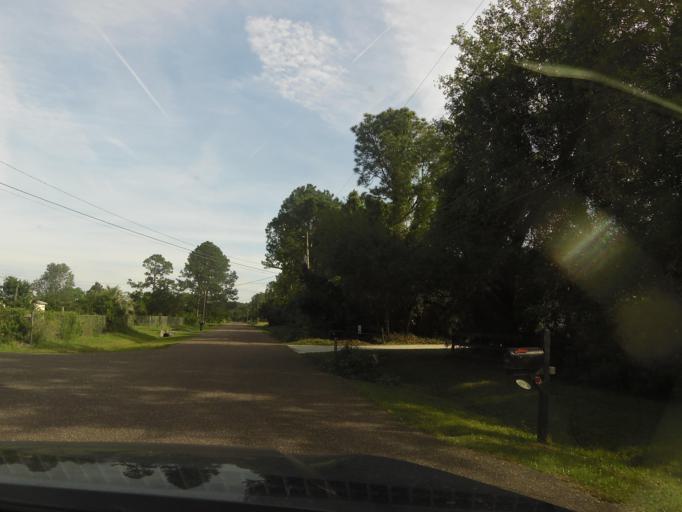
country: US
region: Florida
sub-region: Nassau County
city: Fernandina Beach
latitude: 30.5317
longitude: -81.4885
